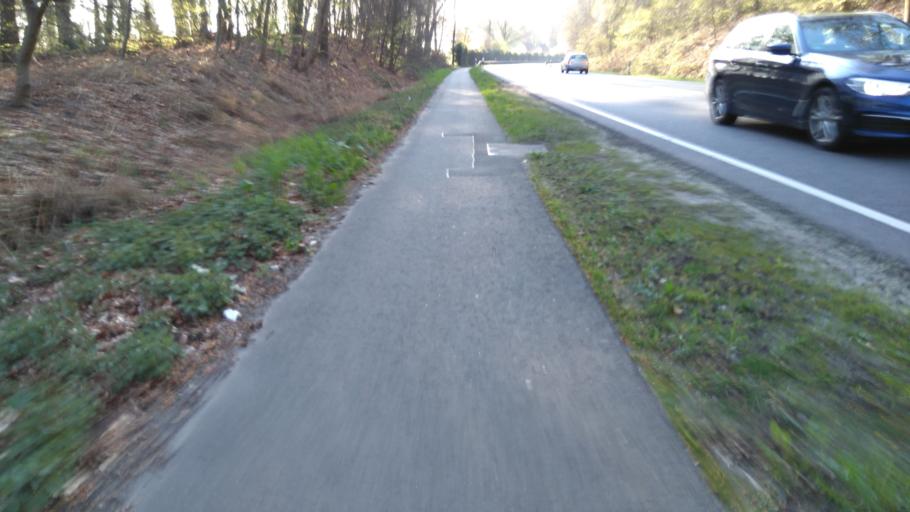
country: DE
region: Lower Saxony
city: Nottensdorf
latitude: 53.4782
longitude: 9.6419
